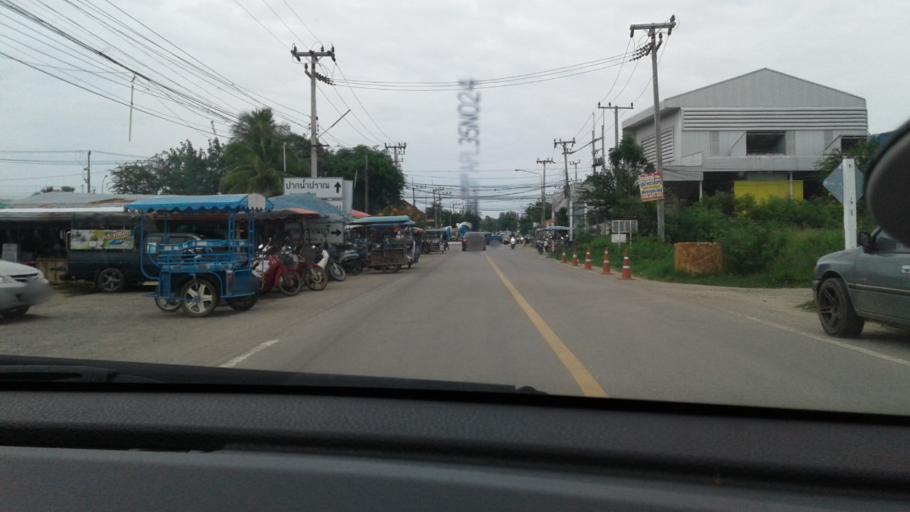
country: TH
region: Prachuap Khiri Khan
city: Pran Buri
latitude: 12.3889
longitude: 99.9853
